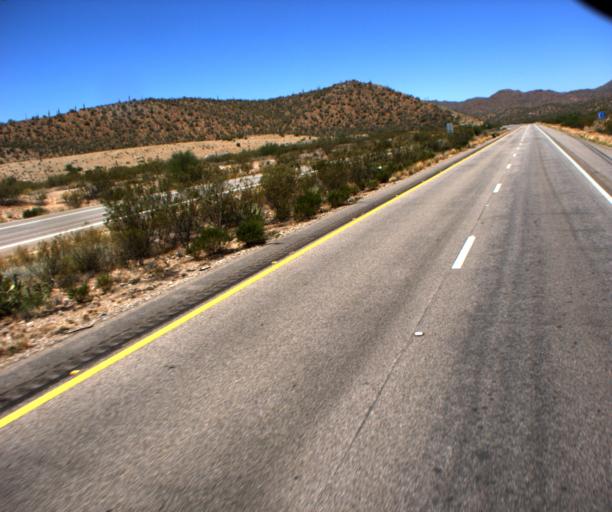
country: US
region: Arizona
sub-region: Yavapai County
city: Bagdad
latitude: 34.3727
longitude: -113.1890
